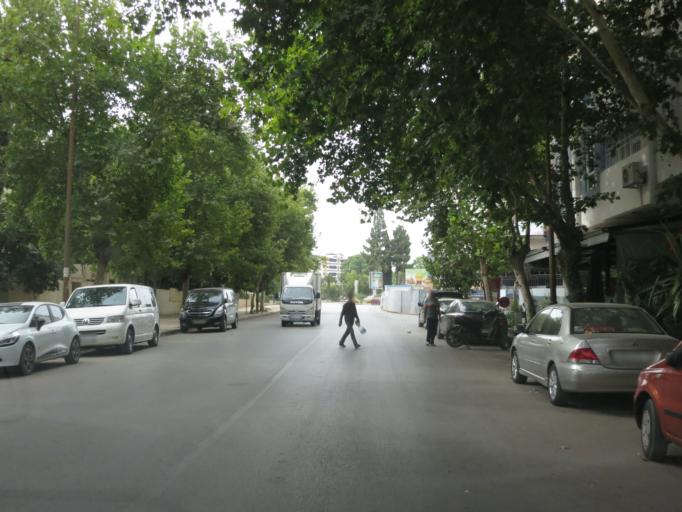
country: MA
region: Fes-Boulemane
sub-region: Fes
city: Fes
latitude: 34.0390
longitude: -5.0038
